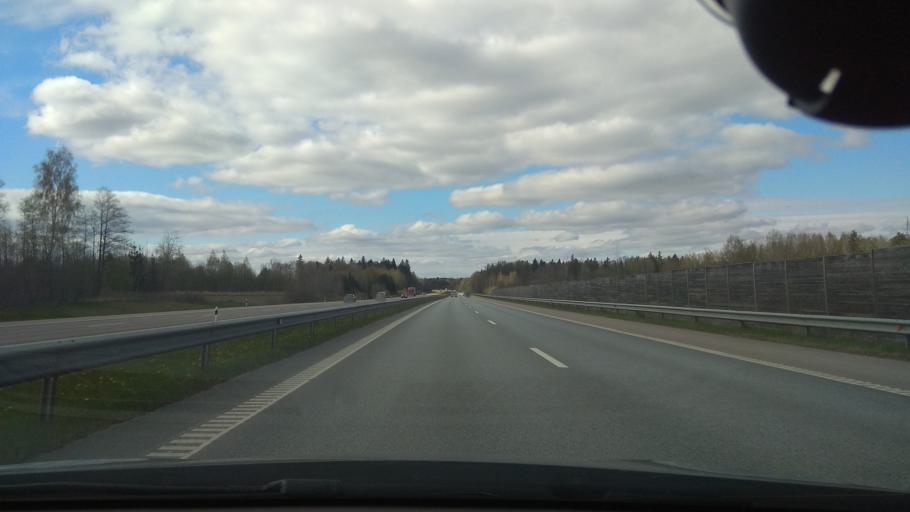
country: LT
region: Vilnius County
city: Pasilaiciai
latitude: 54.8343
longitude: 25.1206
